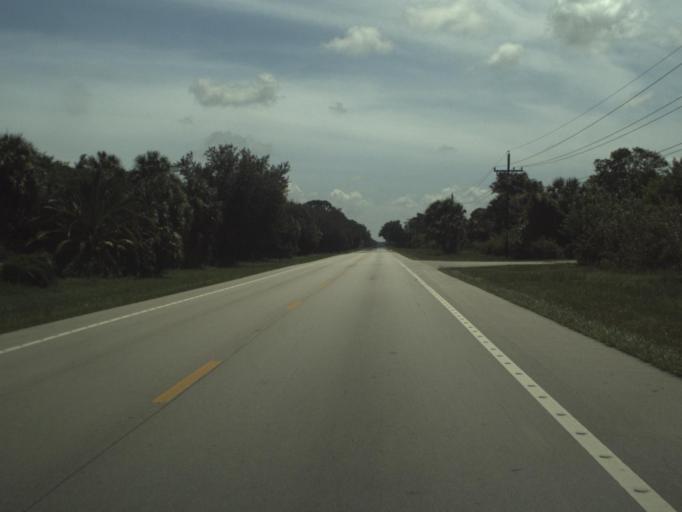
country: US
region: Florida
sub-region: Martin County
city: Indiantown
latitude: 26.9977
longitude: -80.5778
